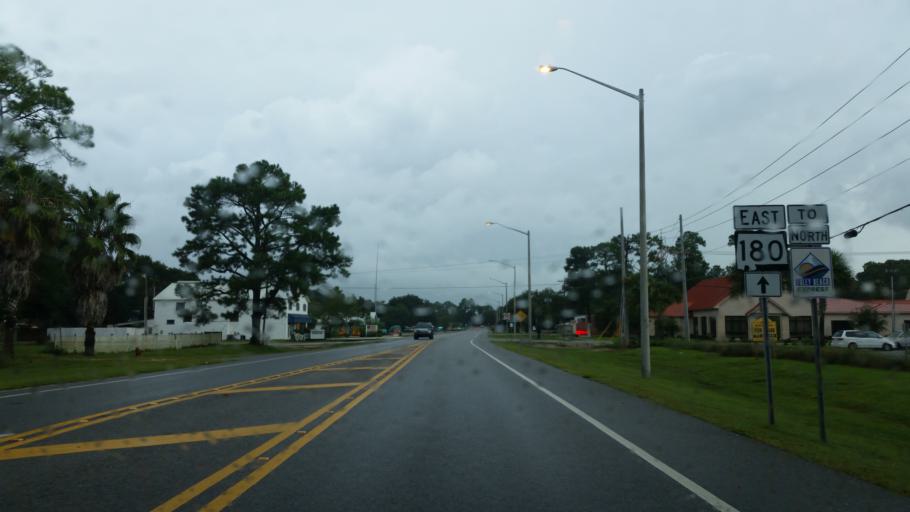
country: US
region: Alabama
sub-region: Baldwin County
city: Gulf Shores
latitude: 30.2747
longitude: -87.6831
